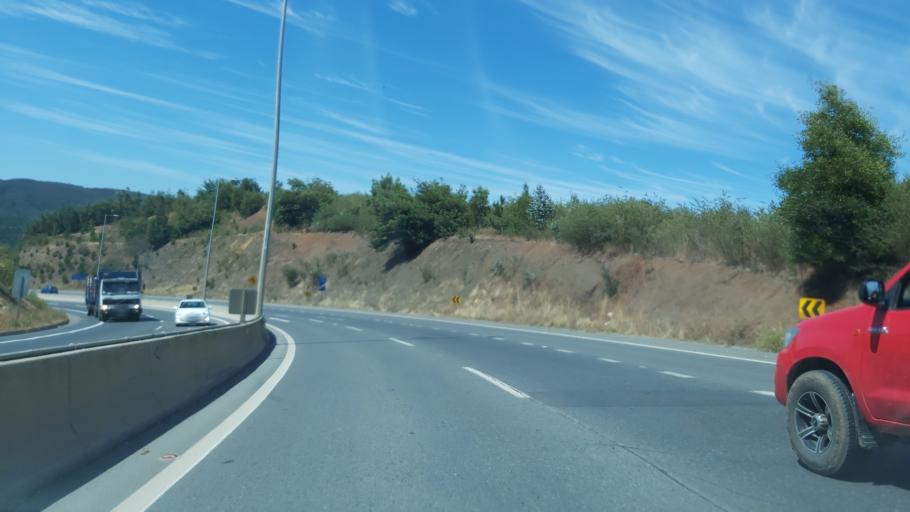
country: CL
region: Biobio
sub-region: Provincia de Concepcion
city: Lota
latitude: -37.1006
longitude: -73.1496
